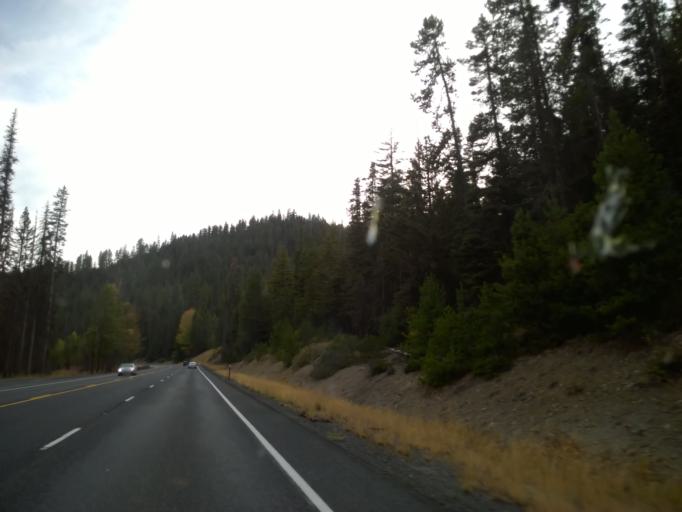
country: US
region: Washington
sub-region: Chelan County
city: Cashmere
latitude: 47.3528
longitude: -120.5688
